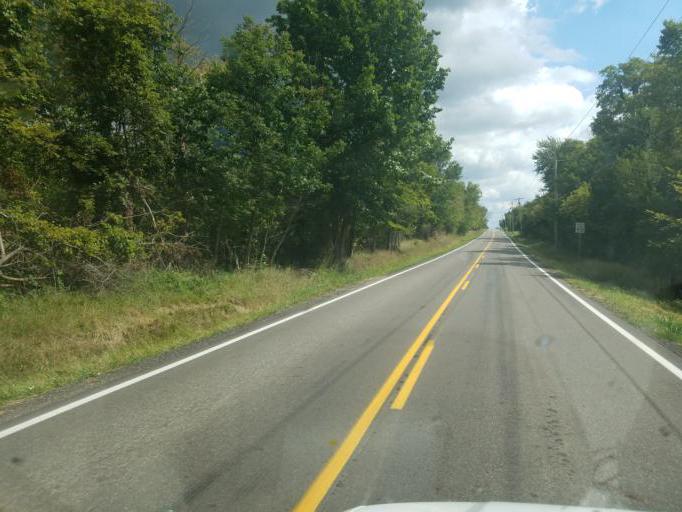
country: US
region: Ohio
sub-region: Huron County
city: Greenwich
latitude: 40.9241
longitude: -82.5257
